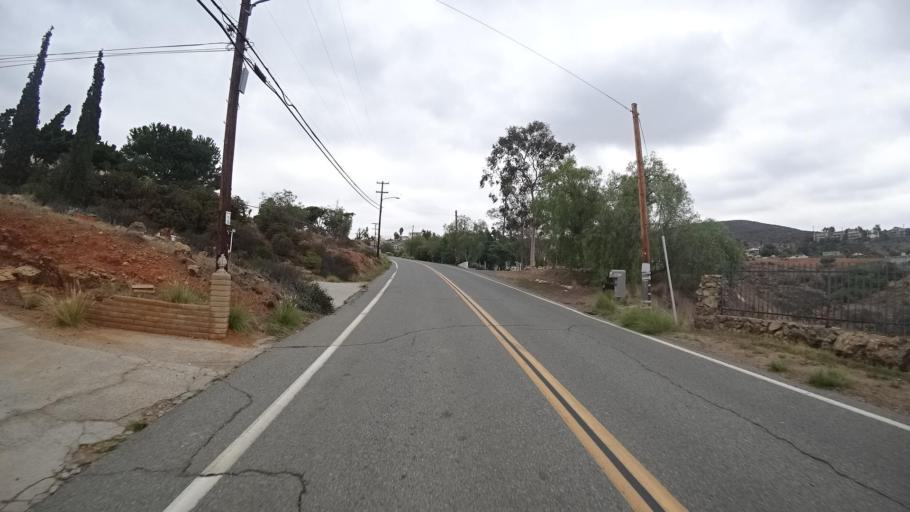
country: US
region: California
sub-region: San Diego County
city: Spring Valley
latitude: 32.7318
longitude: -117.0003
